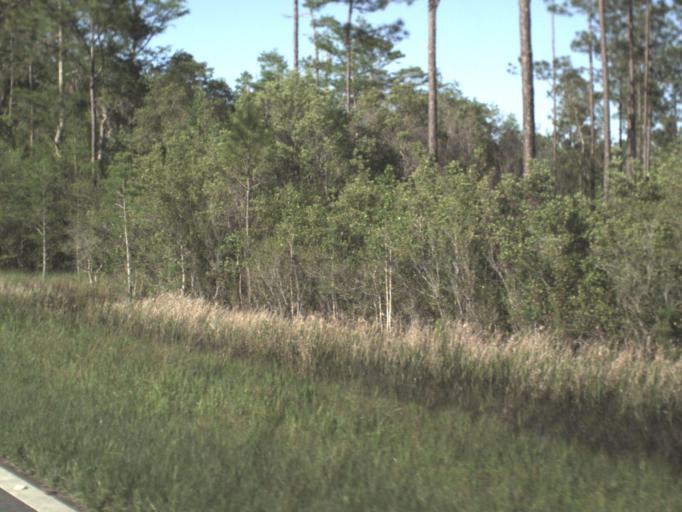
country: US
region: Florida
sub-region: Liberty County
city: Bristol
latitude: 30.3058
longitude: -84.8308
